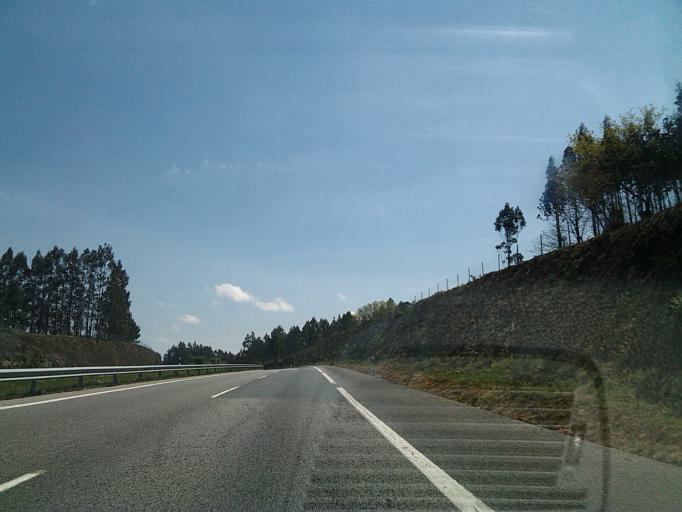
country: ES
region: Galicia
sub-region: Provincia da Coruna
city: Oroso
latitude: 42.9106
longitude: -8.4528
